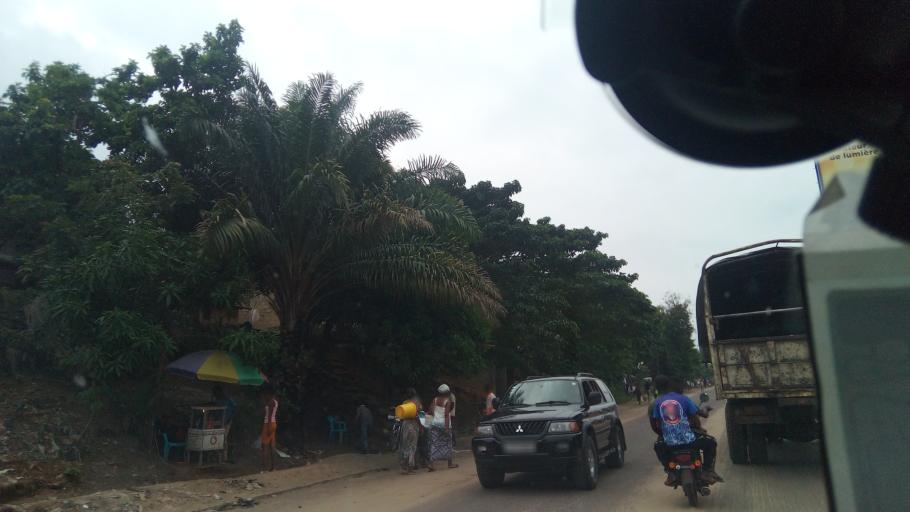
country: CG
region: Brazzaville
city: Brazzaville
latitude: -4.0574
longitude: 15.5540
